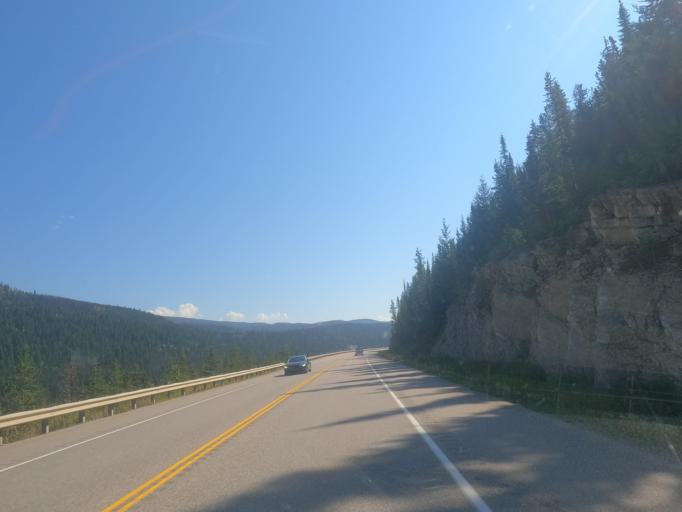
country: CA
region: Alberta
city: Jasper Park Lodge
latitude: 52.8728
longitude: -118.2876
